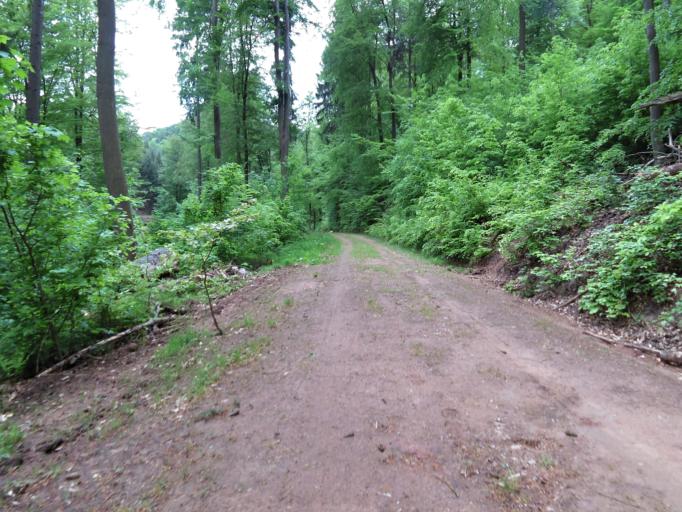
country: DE
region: Rheinland-Pfalz
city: Neidenfels
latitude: 49.4135
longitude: 8.0502
